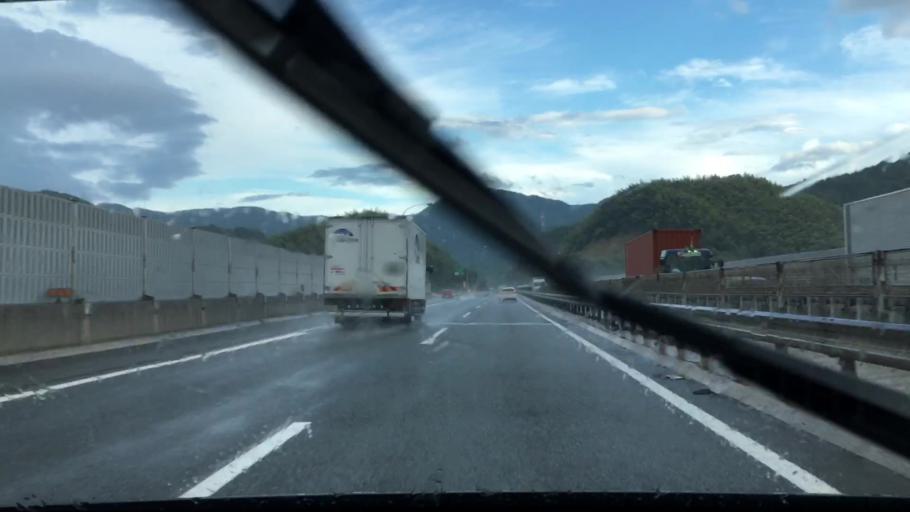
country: JP
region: Fukuoka
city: Kitakyushu
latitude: 33.8052
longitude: 130.8498
